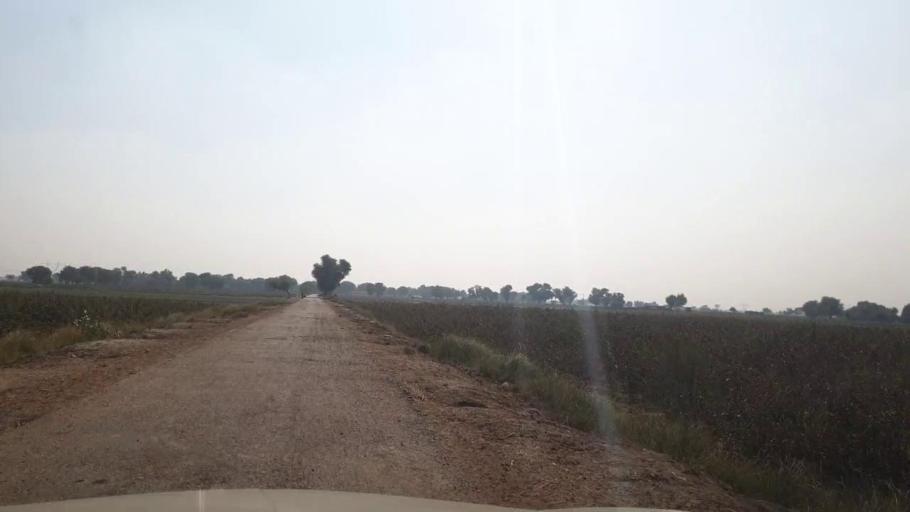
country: PK
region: Sindh
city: Bhan
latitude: 26.5357
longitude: 67.7632
